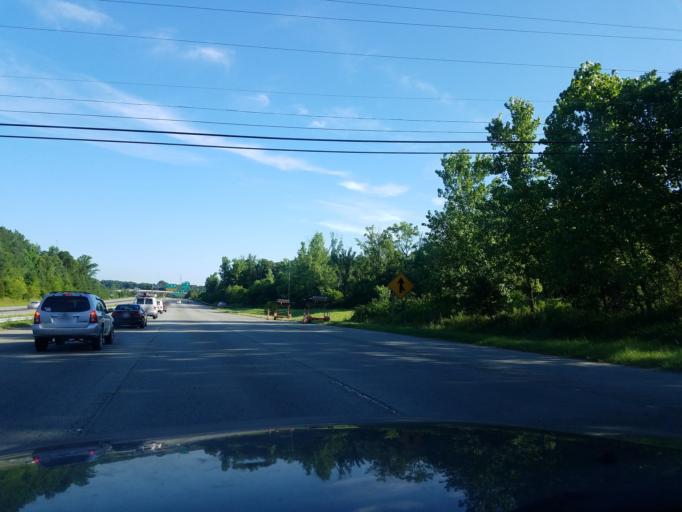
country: US
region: North Carolina
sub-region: Durham County
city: Durham
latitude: 36.0057
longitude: -78.8644
